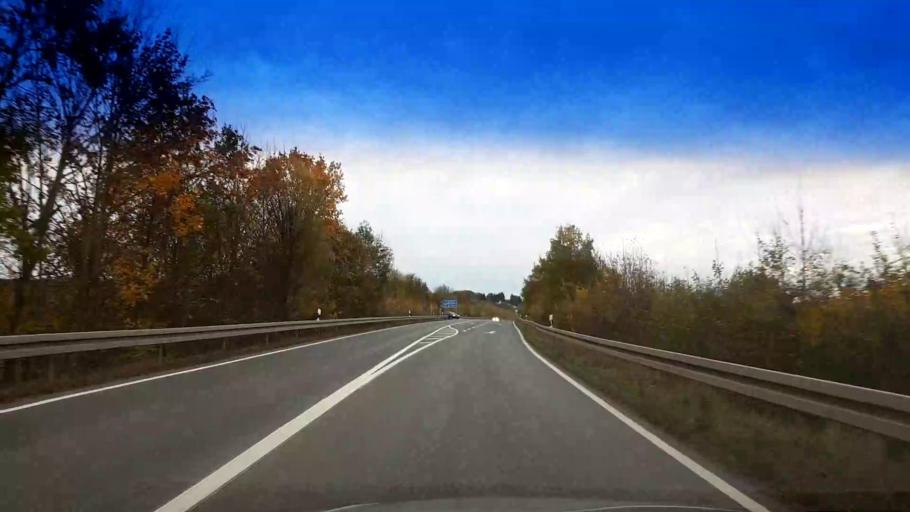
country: DE
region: Bavaria
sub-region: Upper Franconia
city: Viereth-Trunstadt
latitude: 49.9302
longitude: 10.7766
